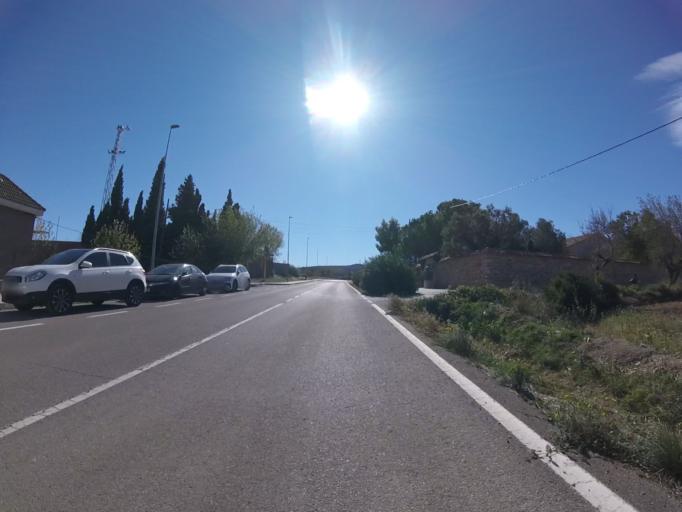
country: ES
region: Valencia
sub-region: Provincia de Castello
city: Albocasser
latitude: 40.3643
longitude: 0.0211
